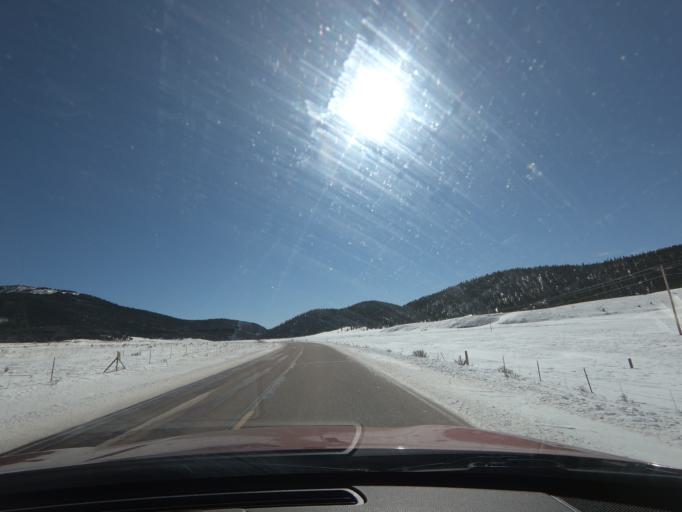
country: US
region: Colorado
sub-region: Teller County
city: Cripple Creek
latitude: 38.7645
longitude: -105.1160
